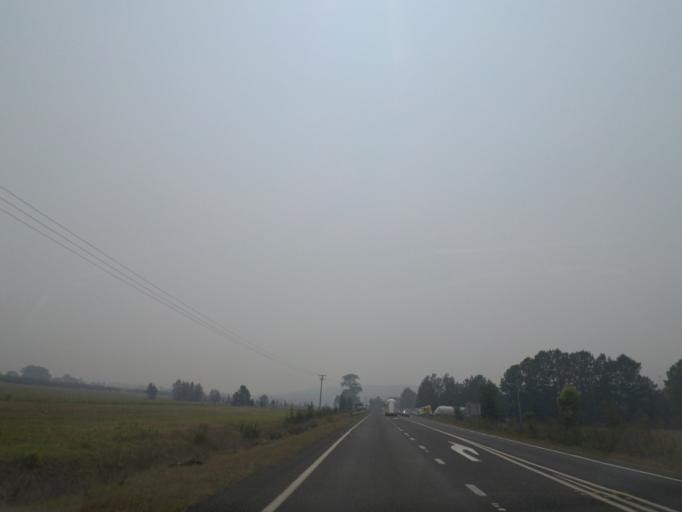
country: AU
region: New South Wales
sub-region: Clarence Valley
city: Maclean
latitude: -29.5662
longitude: 153.1367
